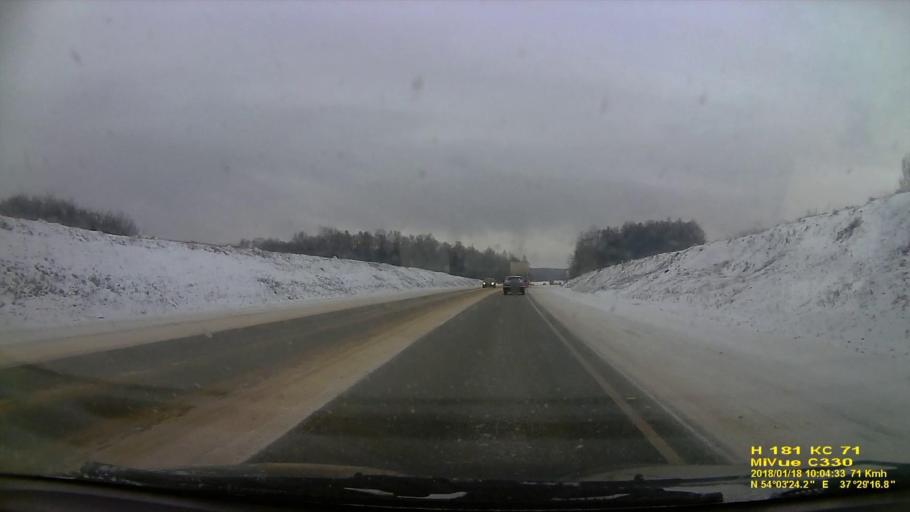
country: RU
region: Tula
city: Pervomayskiy
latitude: 54.0566
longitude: 37.4881
